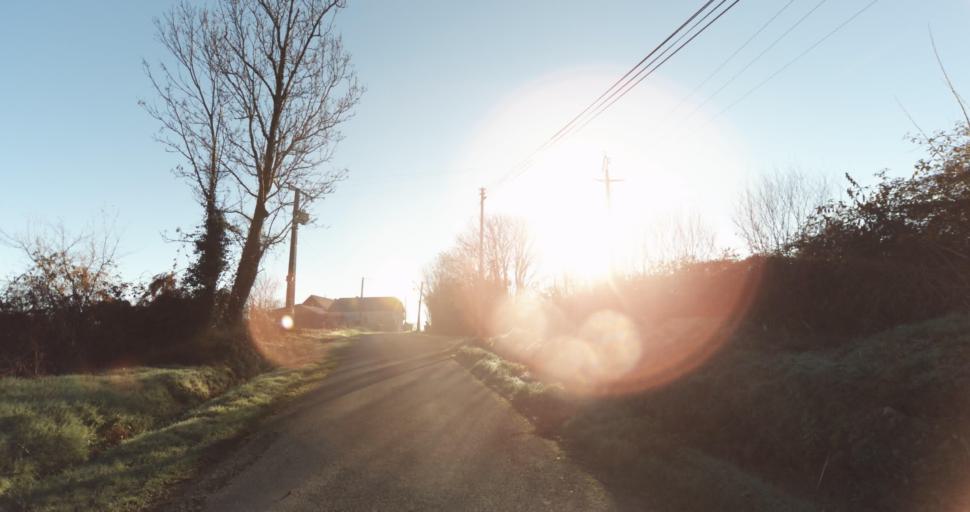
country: FR
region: Aquitaine
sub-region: Departement des Pyrenees-Atlantiques
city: Ousse
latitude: 43.3113
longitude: -0.2374
